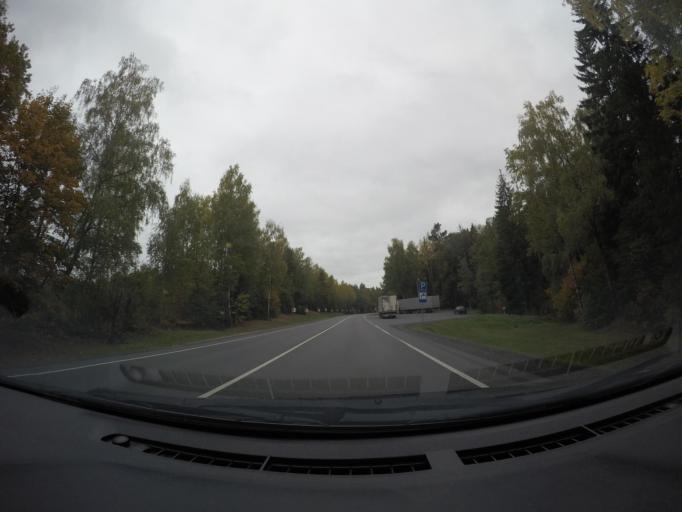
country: RU
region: Moskovskaya
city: Ruza
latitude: 55.7531
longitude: 36.2582
